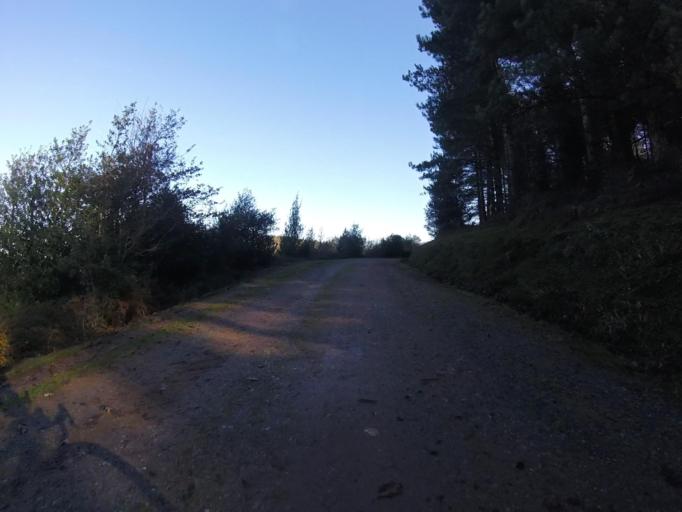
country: ES
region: Navarre
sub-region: Provincia de Navarra
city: Bera
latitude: 43.3190
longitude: -1.6958
